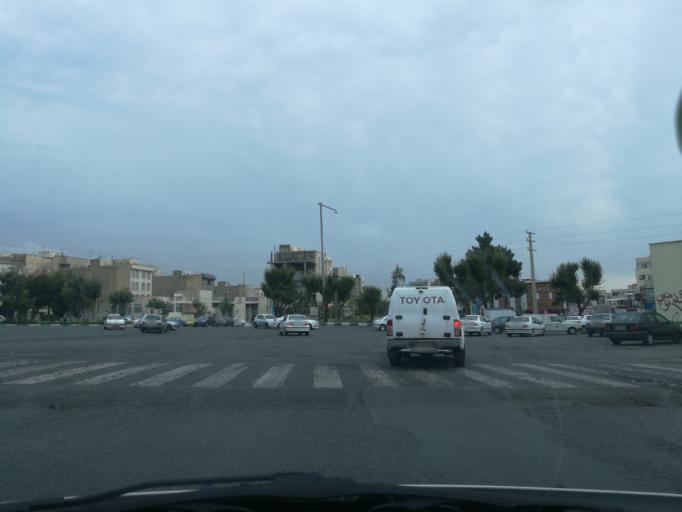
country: IR
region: Alborz
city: Karaj
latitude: 35.8506
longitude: 50.9670
